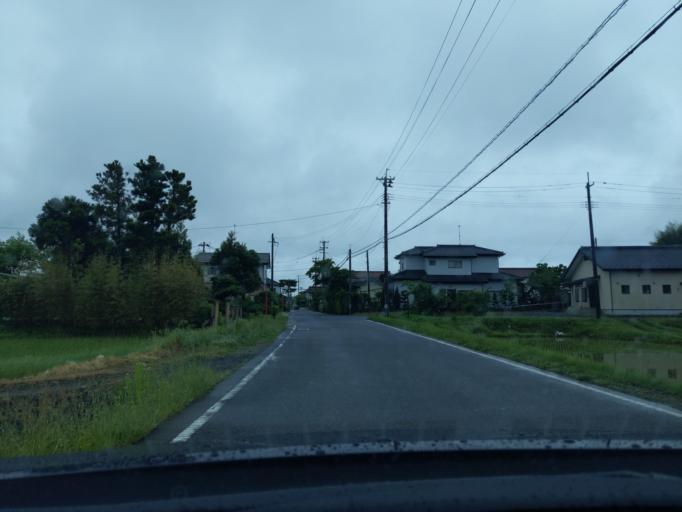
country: JP
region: Fukushima
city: Koriyama
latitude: 37.4219
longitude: 140.3045
